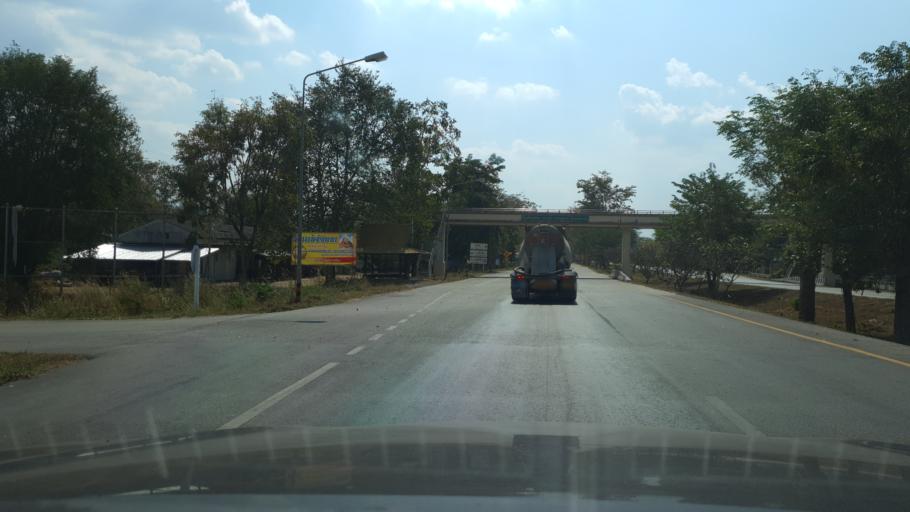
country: TH
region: Lampang
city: Mae Phrik
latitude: 17.4465
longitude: 99.1595
